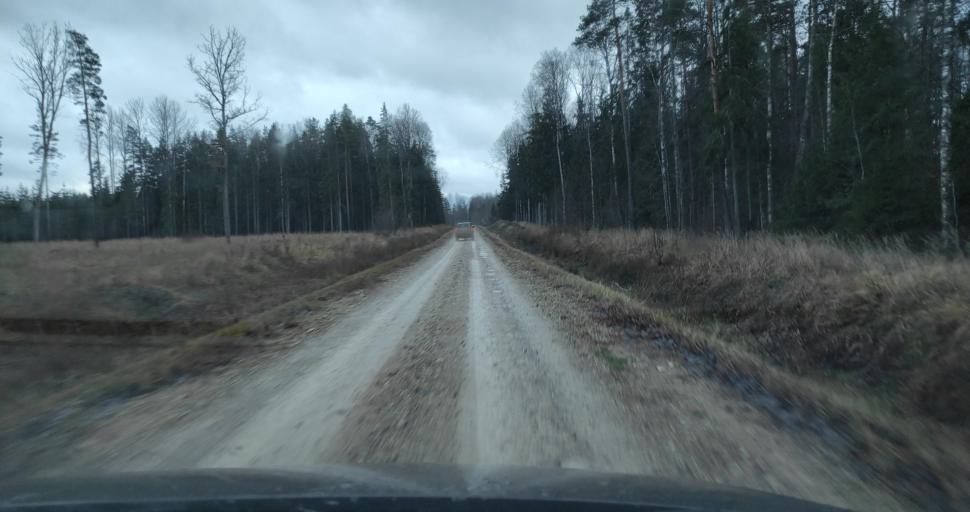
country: LV
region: Skrunda
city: Skrunda
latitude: 56.5579
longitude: 22.0810
